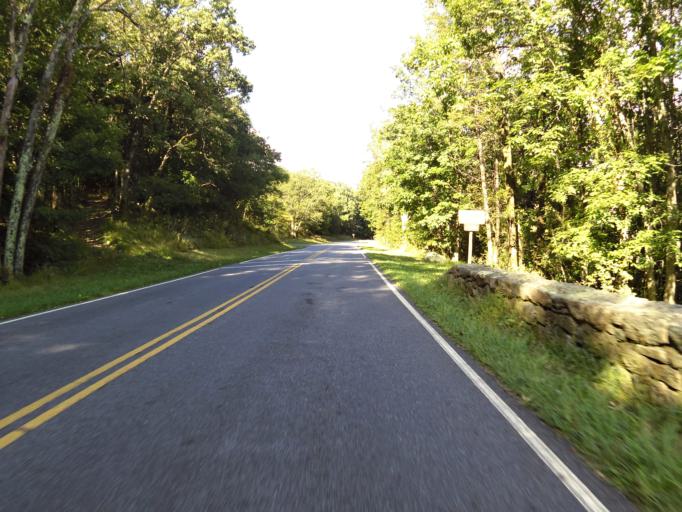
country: US
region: Virginia
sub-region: Page County
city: Stanley
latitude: 38.5317
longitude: -78.4232
